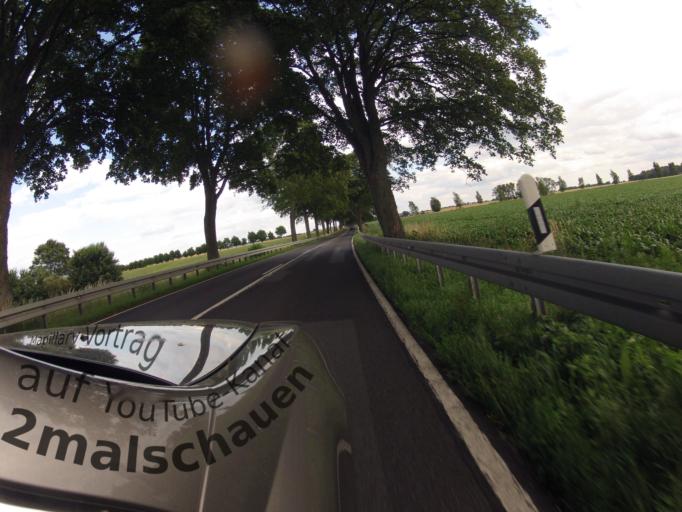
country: DE
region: Mecklenburg-Vorpommern
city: Seebad Bansin
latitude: 53.9033
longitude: 14.0448
